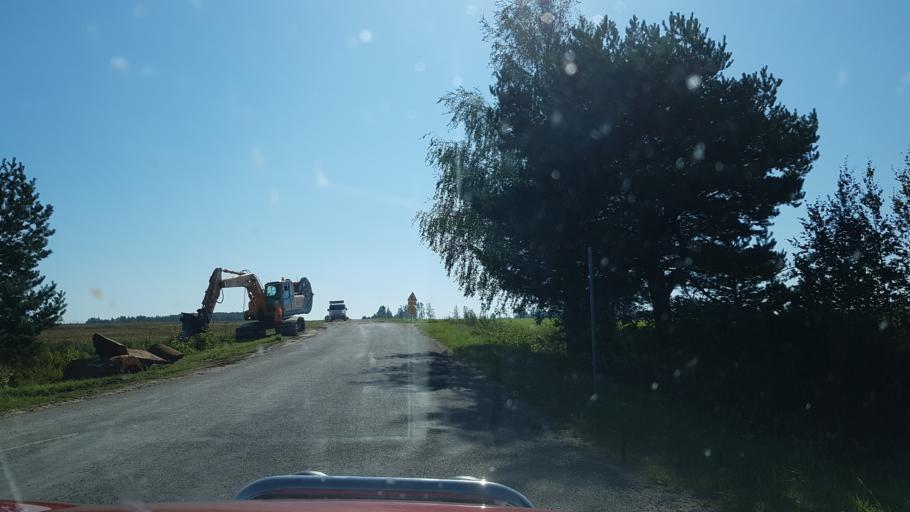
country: EE
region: Tartu
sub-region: UElenurme vald
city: Ulenurme
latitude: 58.2795
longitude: 26.8198
